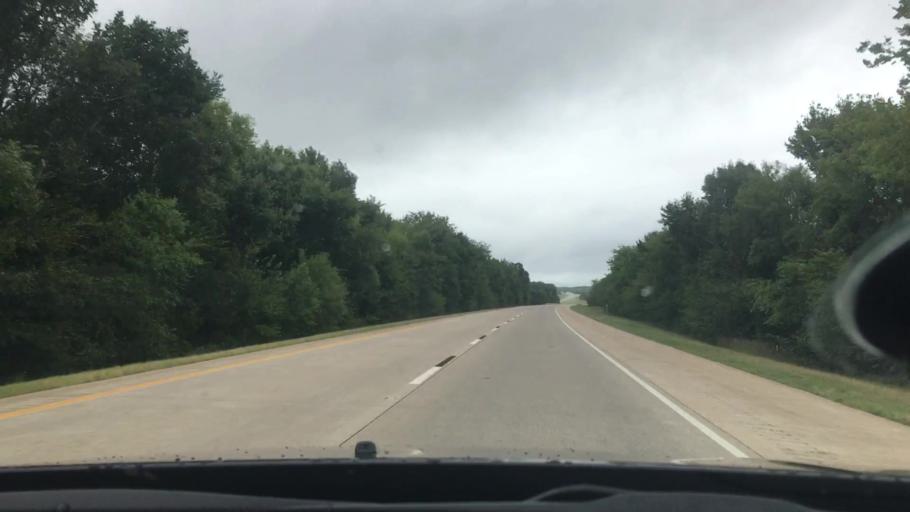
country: US
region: Oklahoma
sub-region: Okmulgee County
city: Henryetta
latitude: 35.4316
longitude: -95.8869
